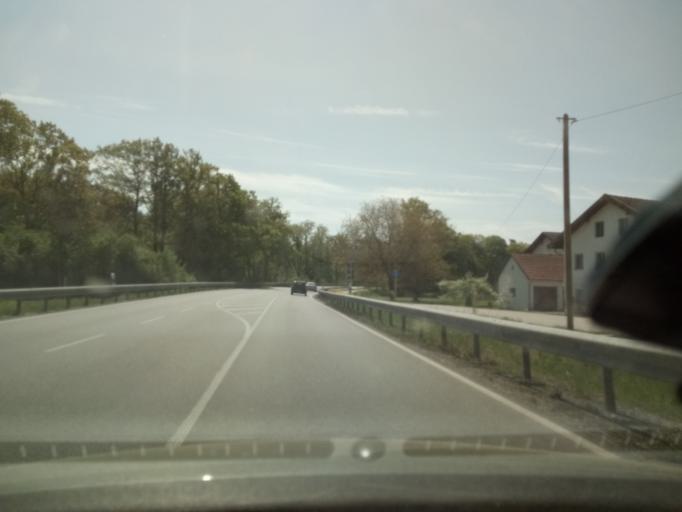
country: DE
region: Bavaria
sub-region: Upper Bavaria
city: Ampfing
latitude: 48.2337
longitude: 12.4137
